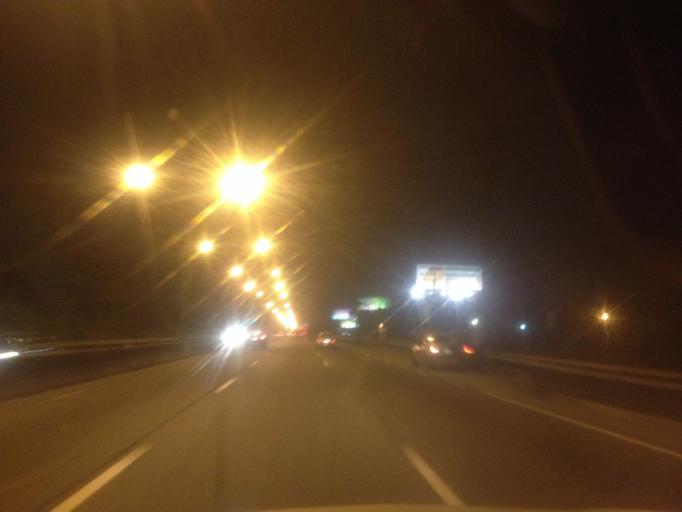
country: BR
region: Rio de Janeiro
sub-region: Duque De Caxias
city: Duque de Caxias
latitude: -22.8024
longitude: -43.3348
